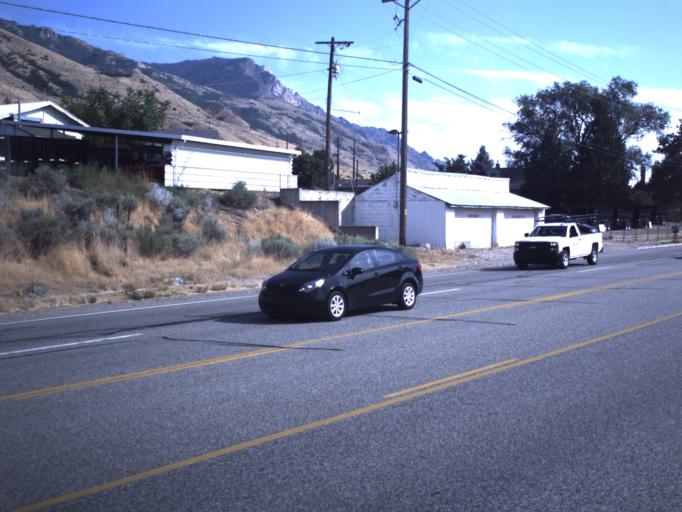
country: US
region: Utah
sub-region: Box Elder County
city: Perry
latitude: 41.4599
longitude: -112.0373
